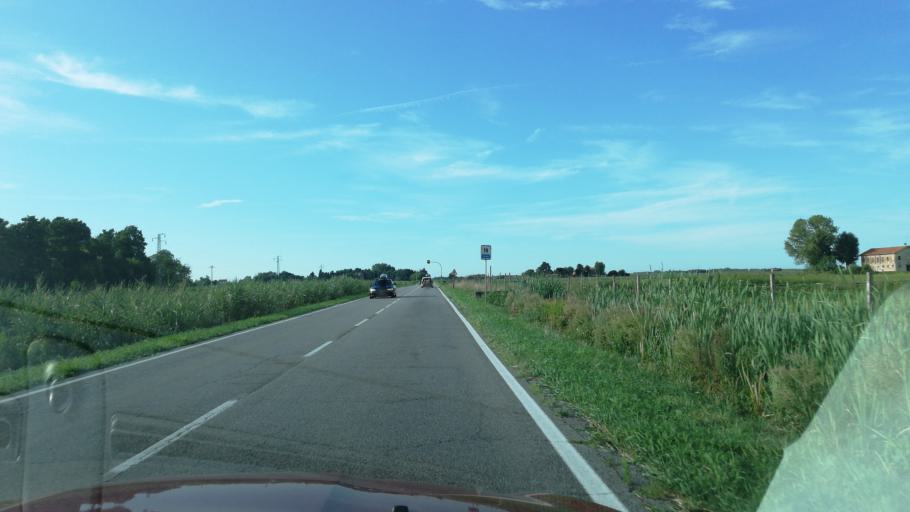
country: IT
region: Veneto
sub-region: Provincia di Venezia
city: La Salute di Livenza
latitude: 45.6101
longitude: 12.8030
